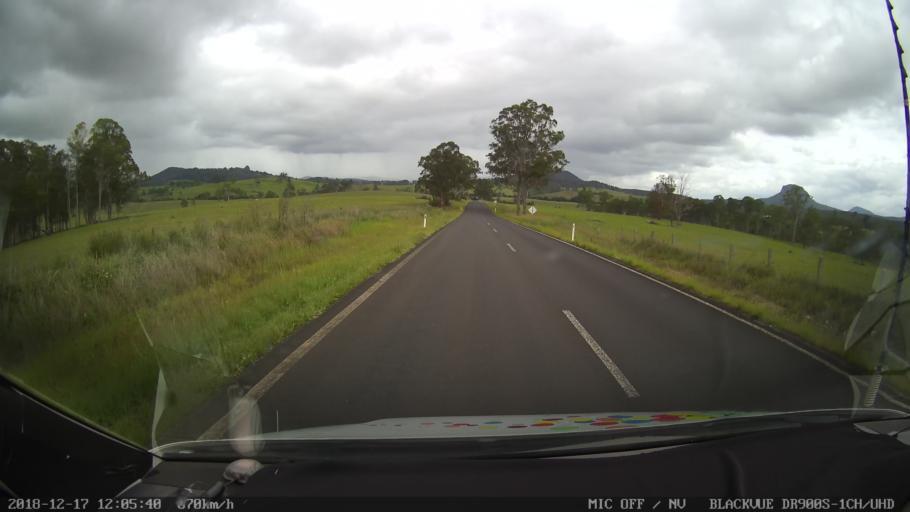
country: AU
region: New South Wales
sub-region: Kyogle
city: Kyogle
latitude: -28.4904
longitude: 152.5666
